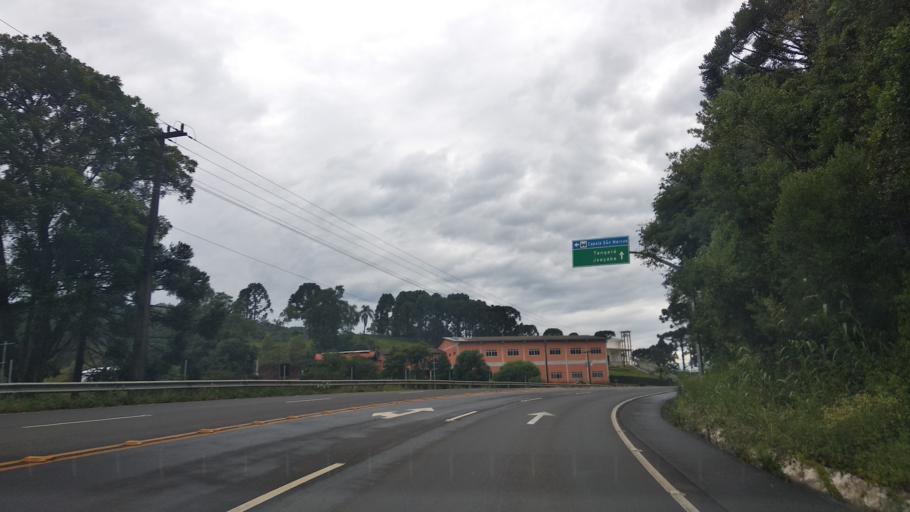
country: BR
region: Santa Catarina
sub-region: Videira
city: Videira
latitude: -27.0772
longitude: -51.2337
